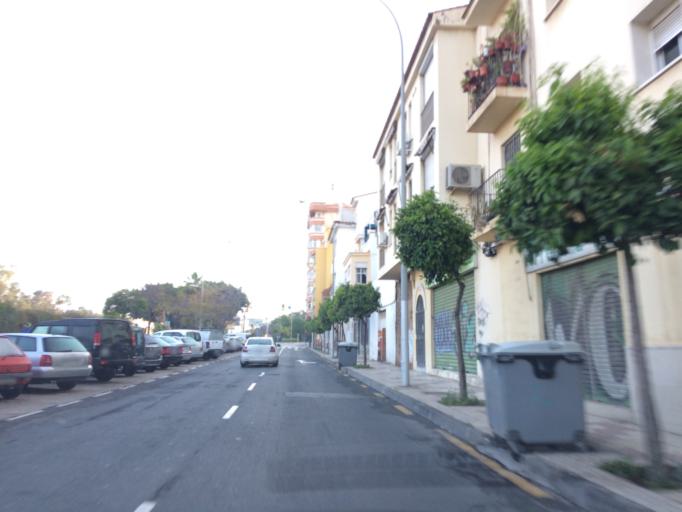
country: ES
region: Andalusia
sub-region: Provincia de Malaga
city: Malaga
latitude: 36.7288
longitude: -4.4255
